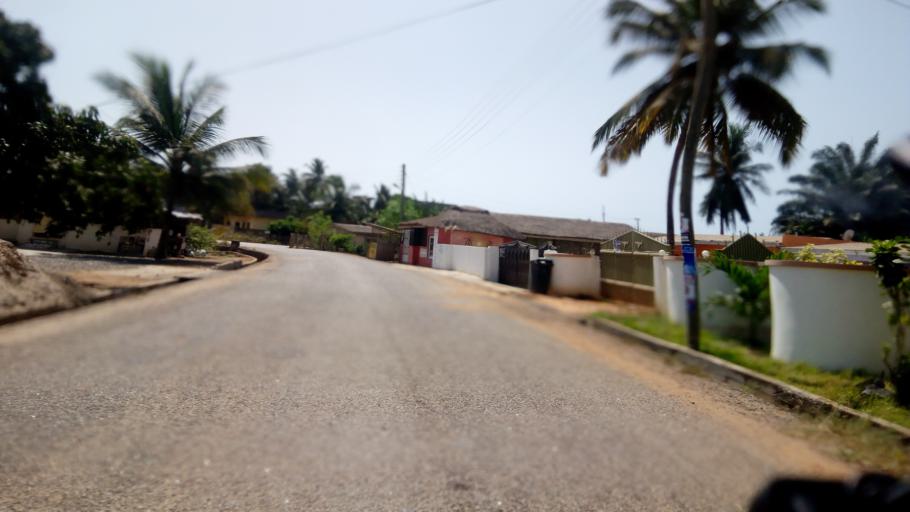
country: GH
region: Central
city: Cape Coast
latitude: 5.1106
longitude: -1.2721
